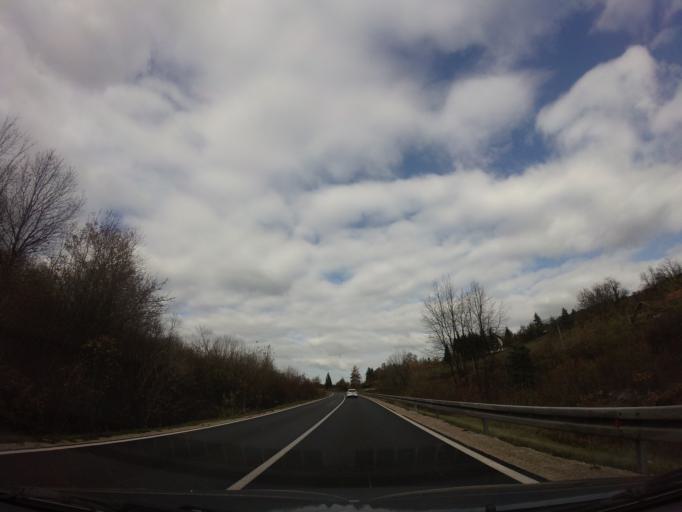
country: HR
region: Karlovacka
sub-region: Grad Karlovac
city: Slunj
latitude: 45.0190
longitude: 15.6512
